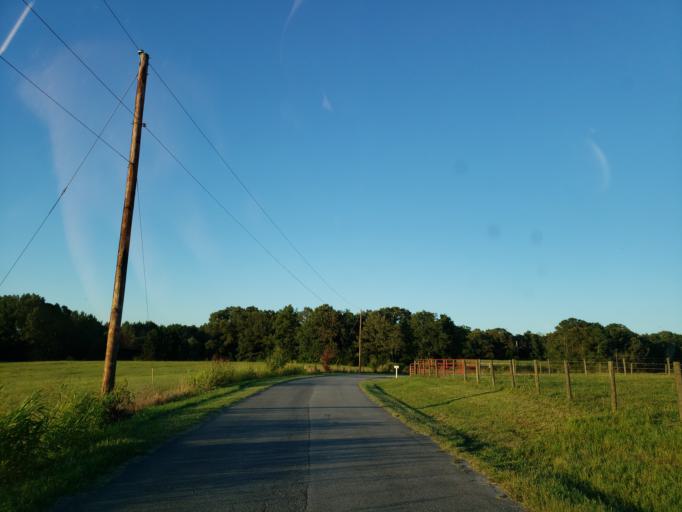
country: US
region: Georgia
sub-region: Bartow County
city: Euharlee
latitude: 34.0809
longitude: -84.9210
